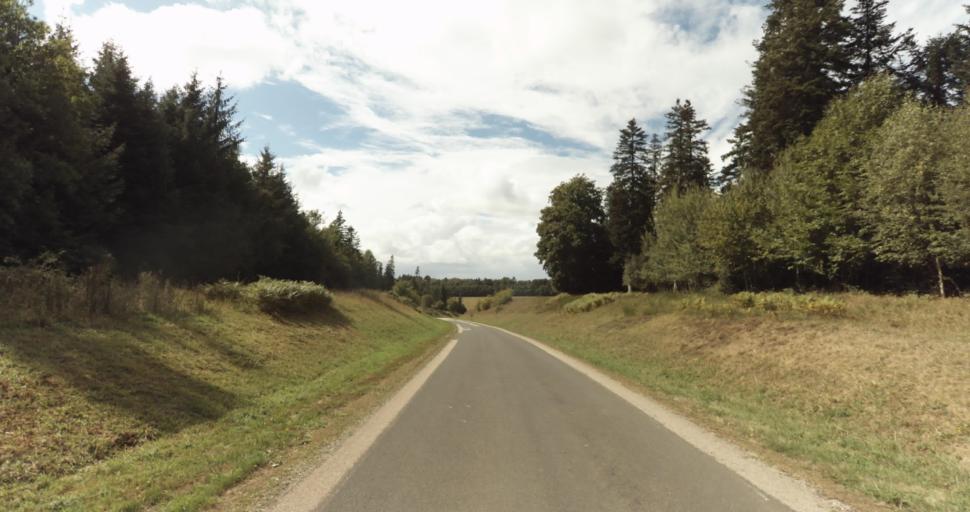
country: FR
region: Lower Normandy
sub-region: Departement de l'Orne
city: Gace
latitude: 48.7831
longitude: 0.3234
